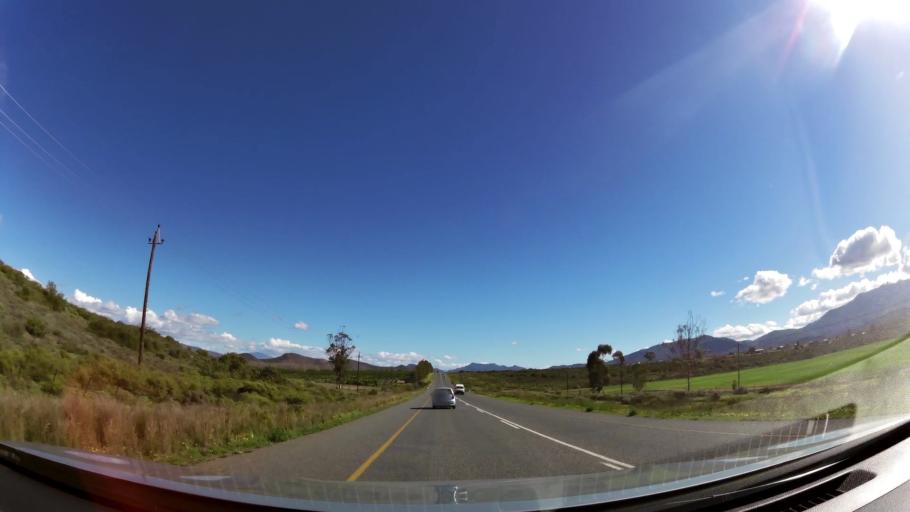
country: ZA
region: Western Cape
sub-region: Cape Winelands District Municipality
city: Ashton
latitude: -33.8144
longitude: 19.9304
